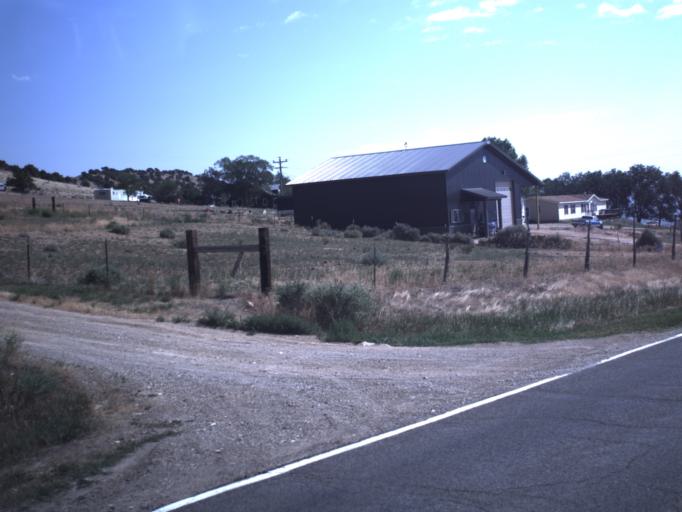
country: US
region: Utah
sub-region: Daggett County
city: Manila
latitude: 40.9772
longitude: -109.7528
